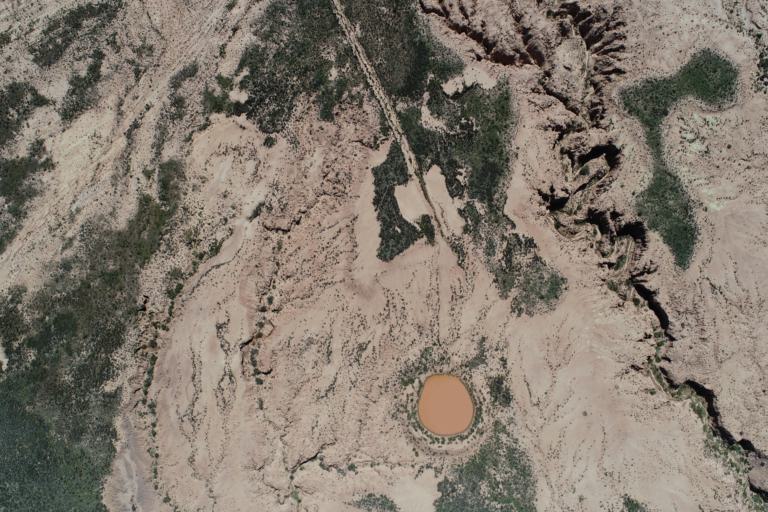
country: BO
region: La Paz
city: Patacamaya
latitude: -17.2936
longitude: -68.4925
